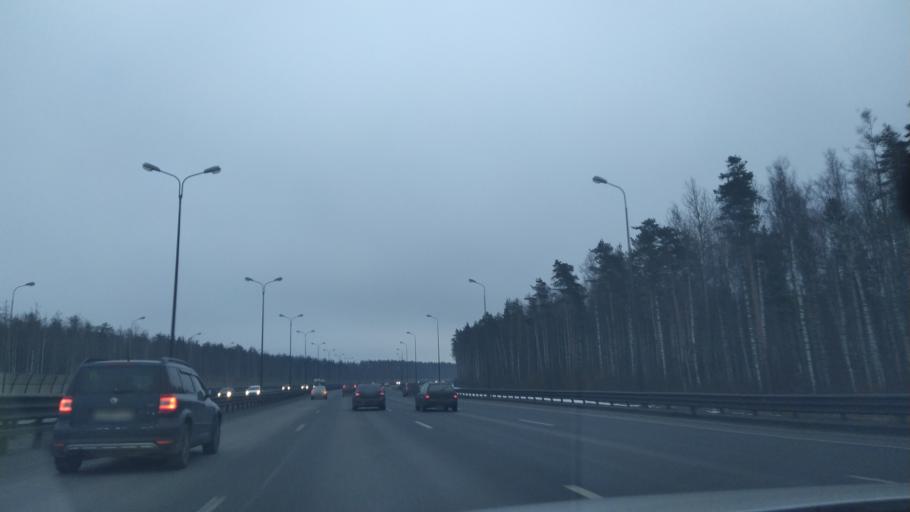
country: RU
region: St.-Petersburg
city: Krasnogvargeisky
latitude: 59.9747
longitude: 30.5398
